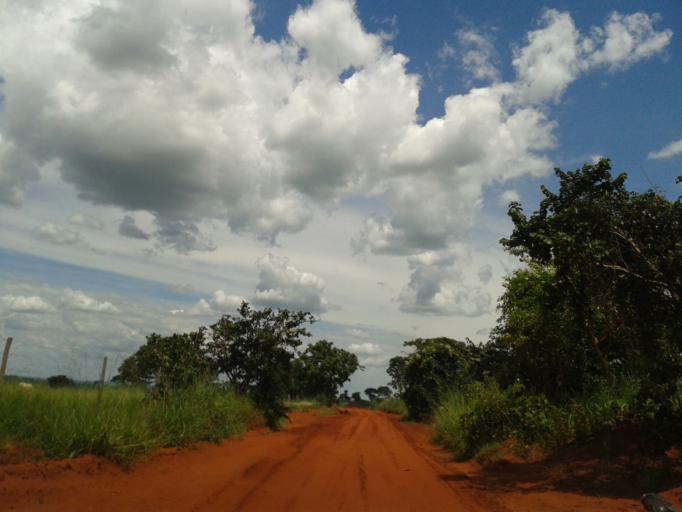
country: BR
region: Minas Gerais
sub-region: Ituiutaba
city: Ituiutaba
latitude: -18.8873
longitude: -49.4695
